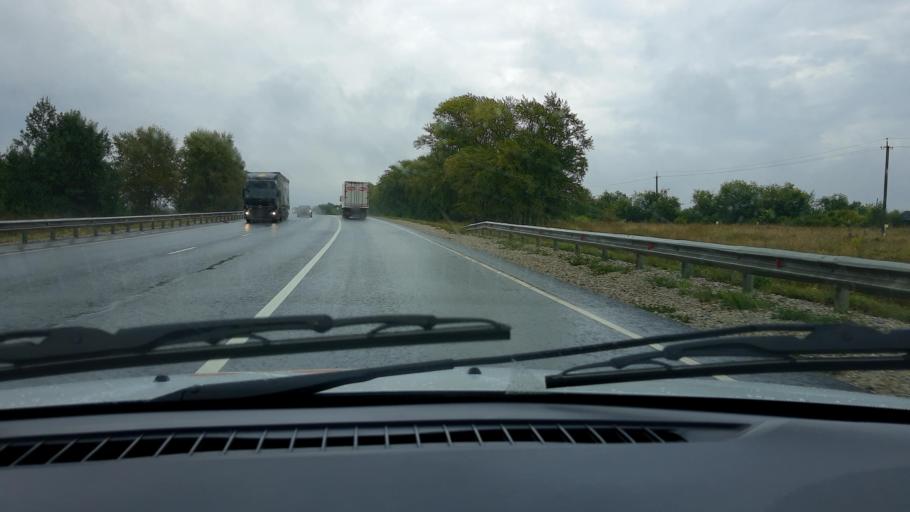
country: RU
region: Chuvashia
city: Tsivil'sk
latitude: 55.7903
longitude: 47.6794
